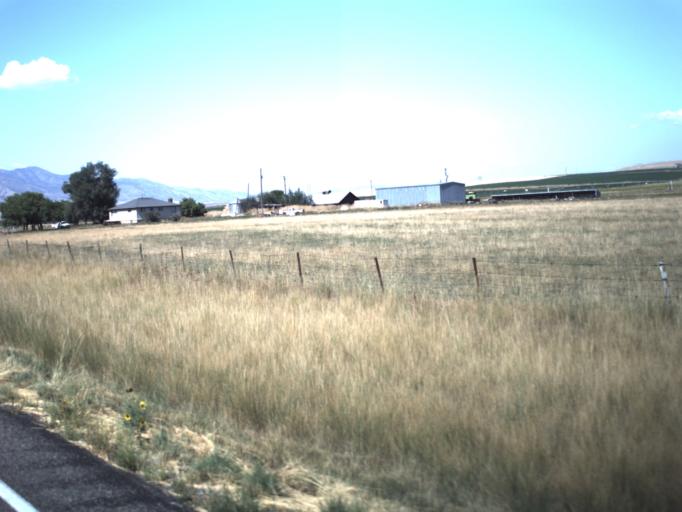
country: US
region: Utah
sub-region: Cache County
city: Benson
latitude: 41.8456
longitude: -111.9648
